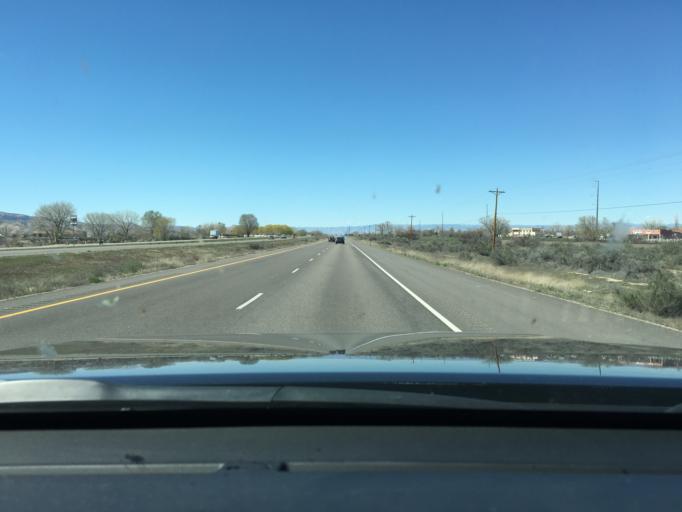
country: US
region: Colorado
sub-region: Mesa County
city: Fruita
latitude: 39.1305
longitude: -108.6870
